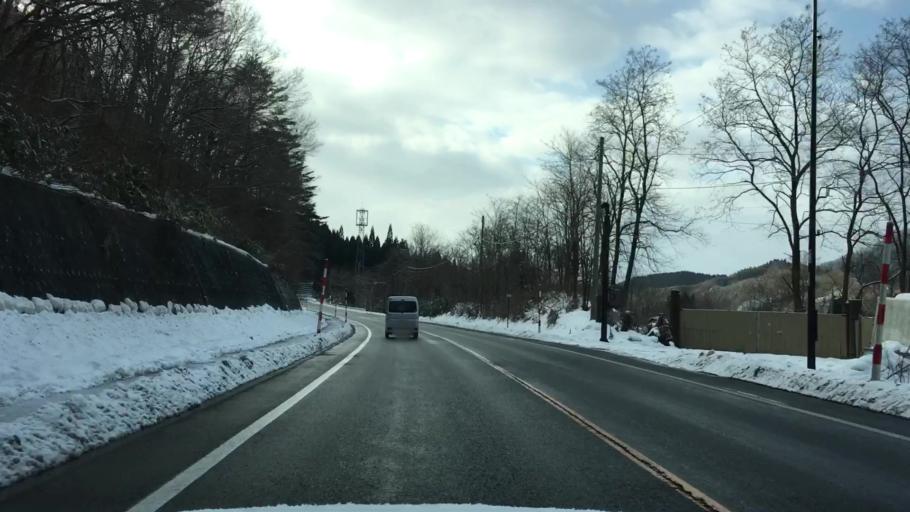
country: JP
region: Akita
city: Odate
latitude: 40.3920
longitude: 140.6050
